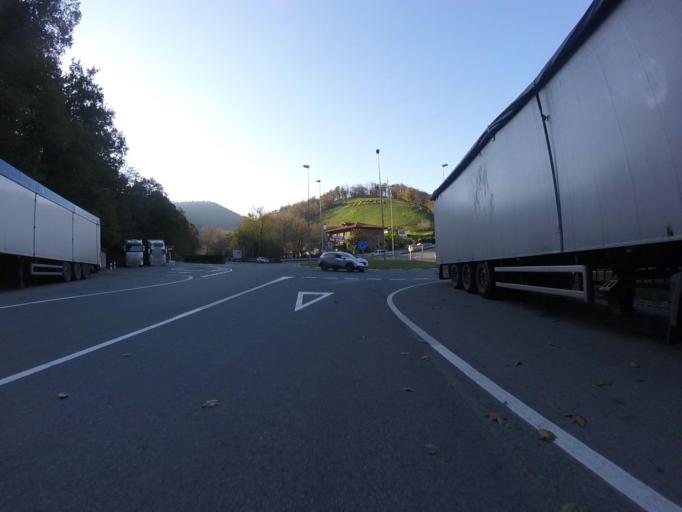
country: ES
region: Navarre
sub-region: Provincia de Navarra
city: Lesaka
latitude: 43.2432
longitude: -1.6699
